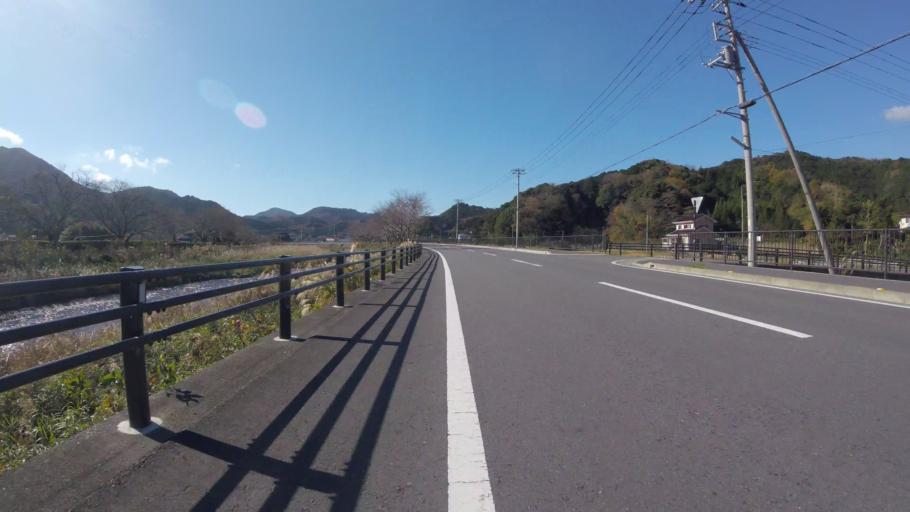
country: JP
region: Shizuoka
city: Shimoda
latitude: 34.7564
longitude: 138.8086
